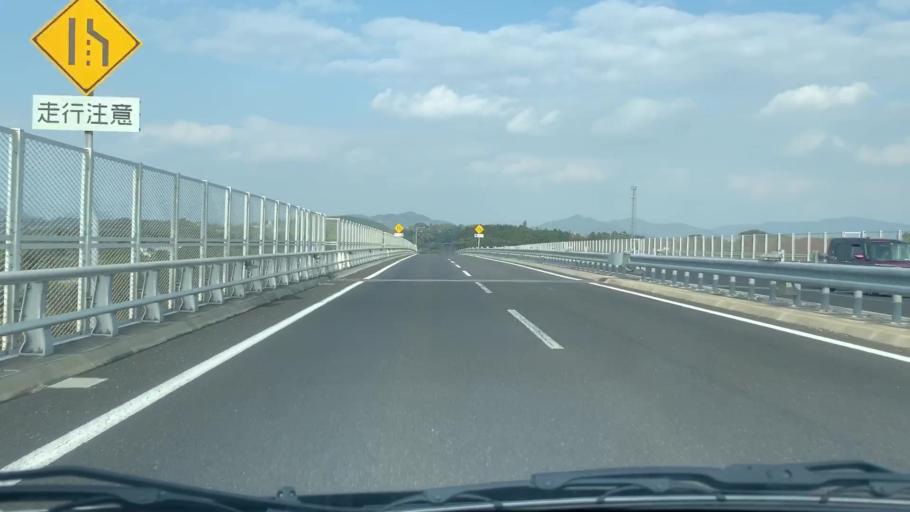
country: JP
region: Nagasaki
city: Sasebo
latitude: 33.0561
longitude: 129.7563
